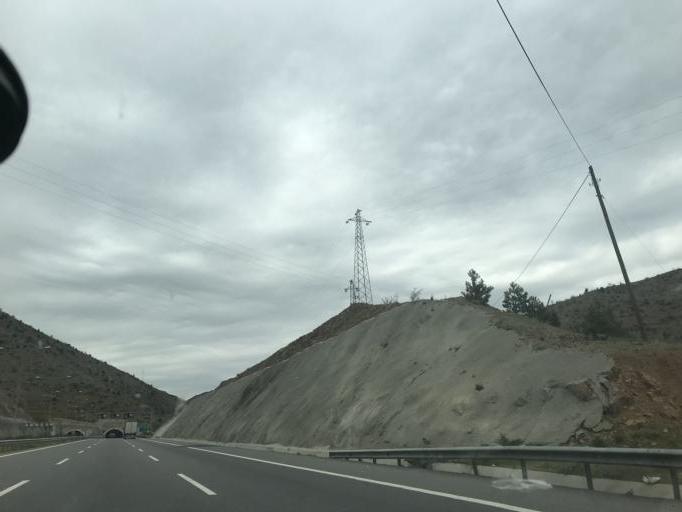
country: TR
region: Nigde
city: Ciftehan
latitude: 37.5698
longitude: 34.7544
